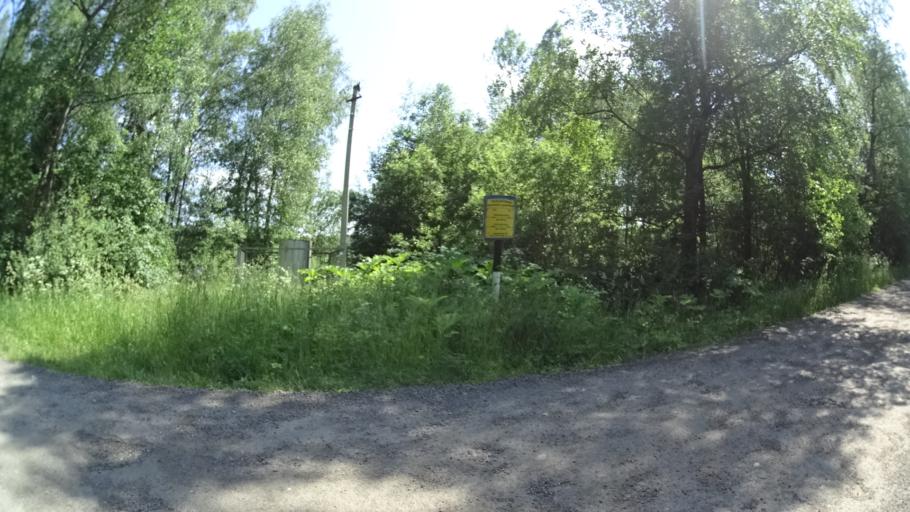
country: RU
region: Moskovskaya
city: Lesnoy
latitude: 56.0818
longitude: 37.9702
